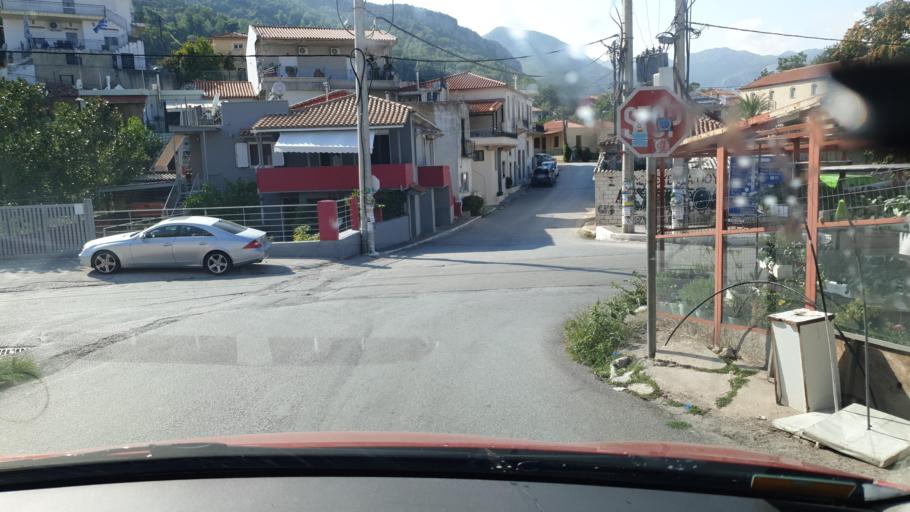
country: GR
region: Central Greece
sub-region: Nomos Evvoias
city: Kymi
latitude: 38.6349
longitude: 24.1030
